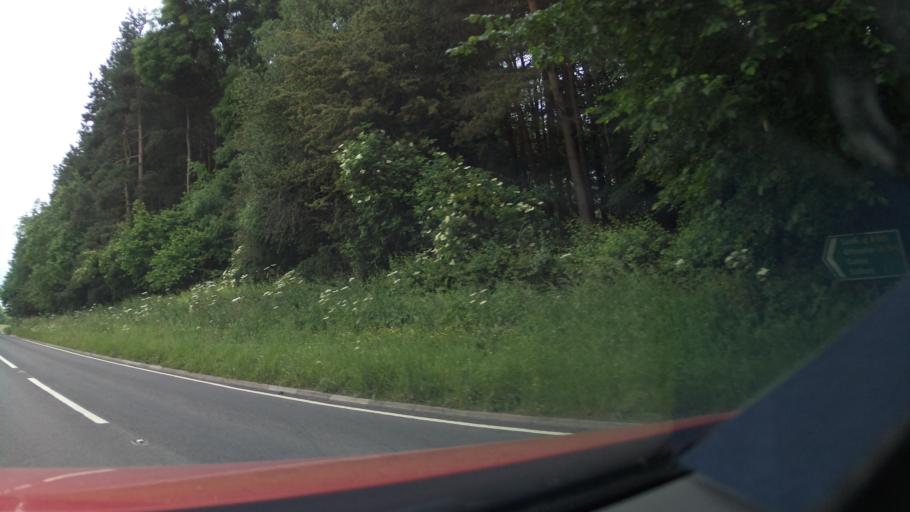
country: GB
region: England
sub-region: Staffordshire
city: Mayfield
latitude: 52.9875
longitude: -1.7467
